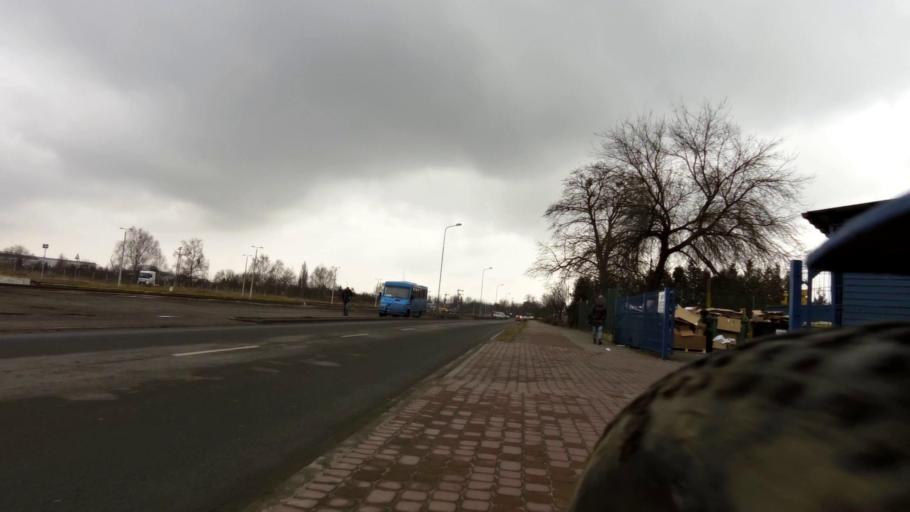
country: PL
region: West Pomeranian Voivodeship
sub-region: Powiat walecki
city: Walcz
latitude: 53.2737
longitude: 16.4842
